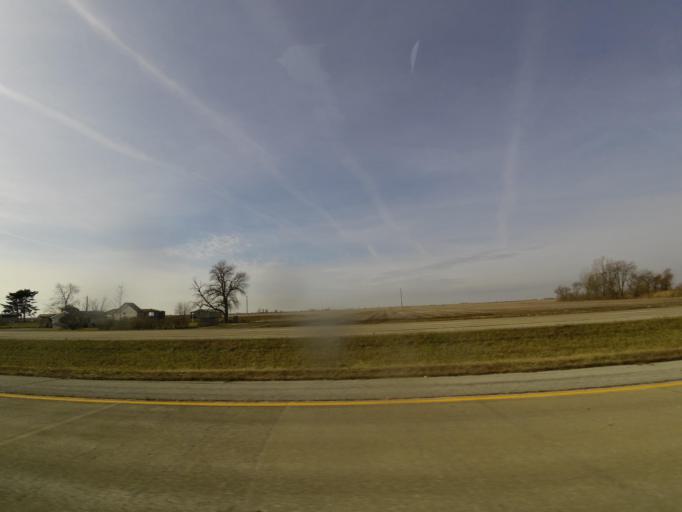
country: US
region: Illinois
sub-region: De Witt County
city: Clinton
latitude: 40.2042
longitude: -88.9604
